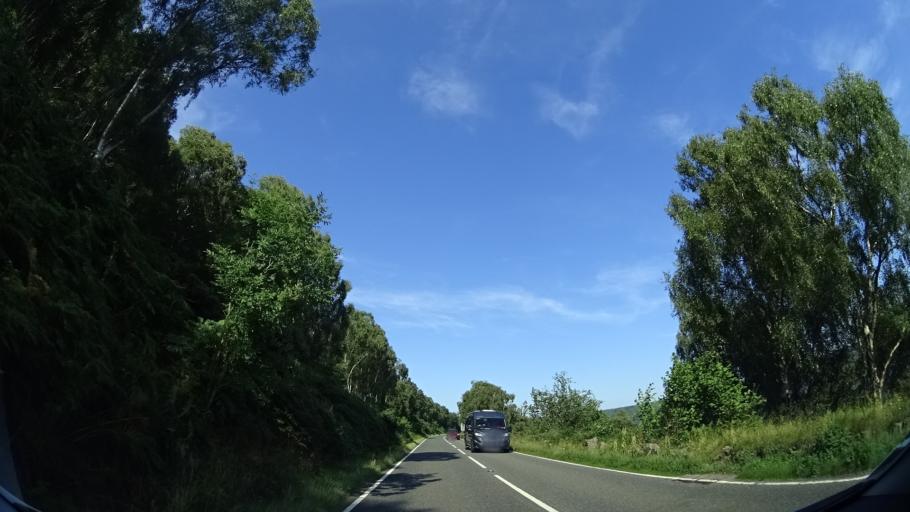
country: GB
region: Scotland
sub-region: Highland
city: Beauly
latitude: 57.3994
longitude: -4.3530
